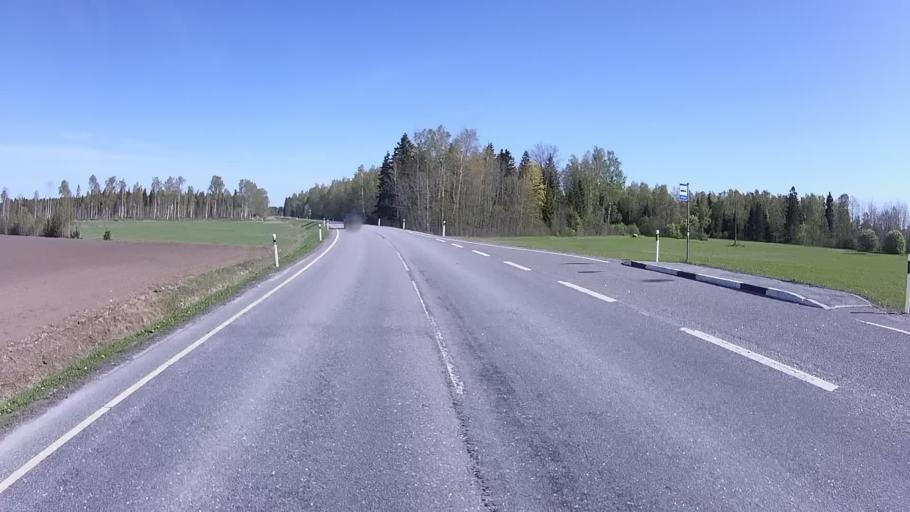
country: EE
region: Raplamaa
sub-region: Rapla vald
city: Rapla
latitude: 58.9463
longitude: 24.7624
